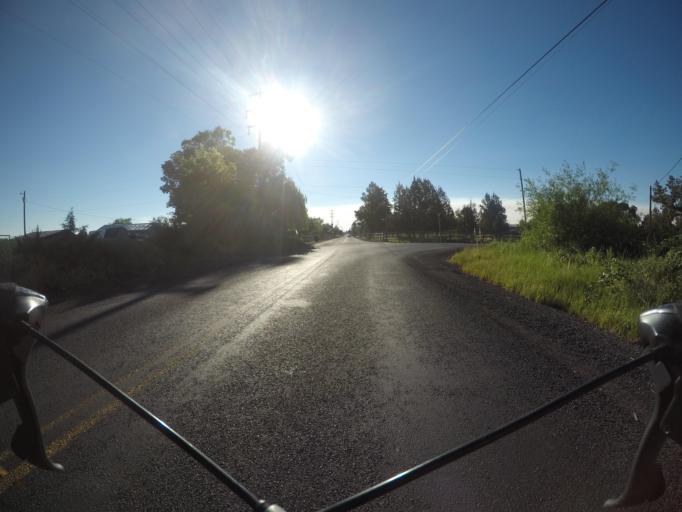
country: US
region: Oregon
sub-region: Deschutes County
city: Redmond
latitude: 44.2620
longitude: -121.2399
